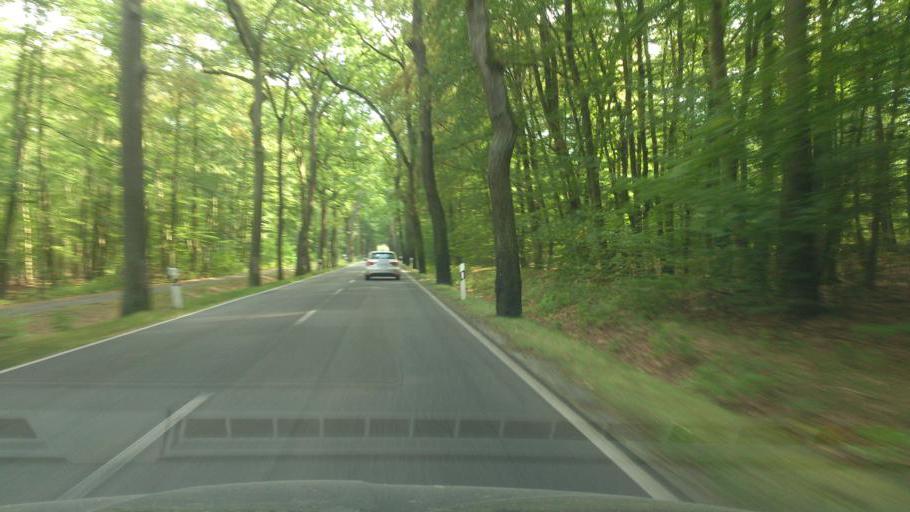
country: DE
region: Berlin
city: Wannsee
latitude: 52.3482
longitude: 13.1511
